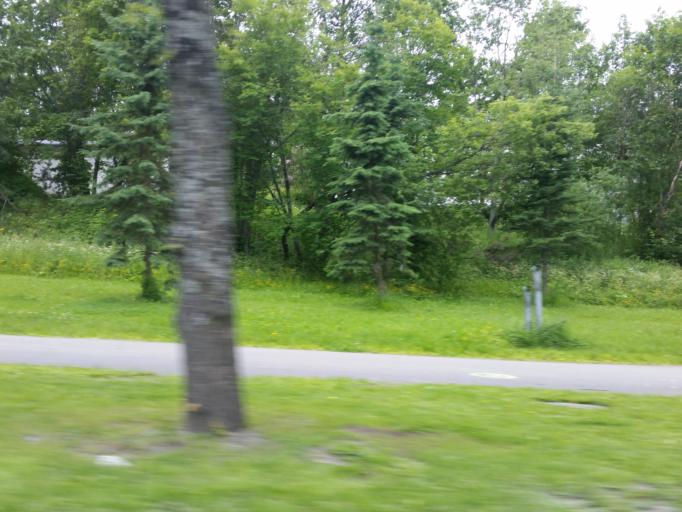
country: FI
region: Northern Savo
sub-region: Kuopio
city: Kuopio
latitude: 62.8862
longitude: 27.6785
